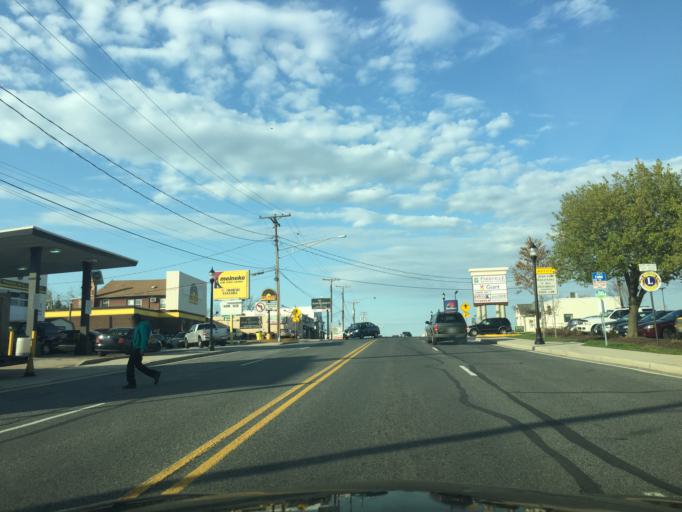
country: US
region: Maryland
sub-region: Baltimore County
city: Parkville
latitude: 39.3720
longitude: -76.5444
